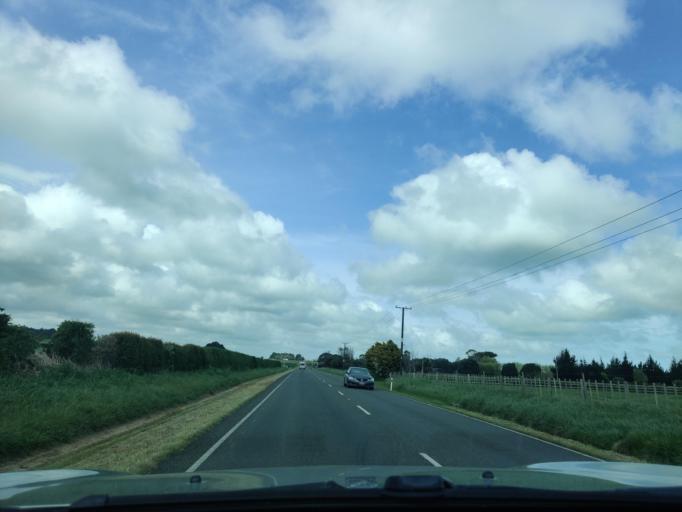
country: NZ
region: Taranaki
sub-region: South Taranaki District
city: Patea
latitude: -39.8101
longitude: 174.7757
